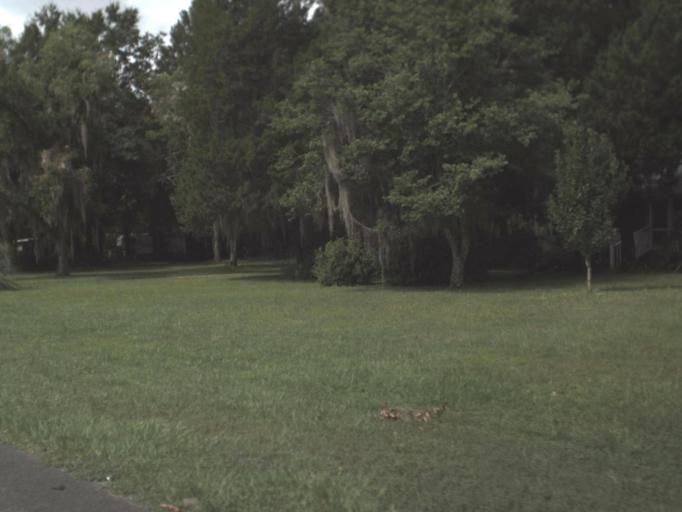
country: US
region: Florida
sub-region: Columbia County
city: Five Points
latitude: 30.3571
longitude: -82.6176
